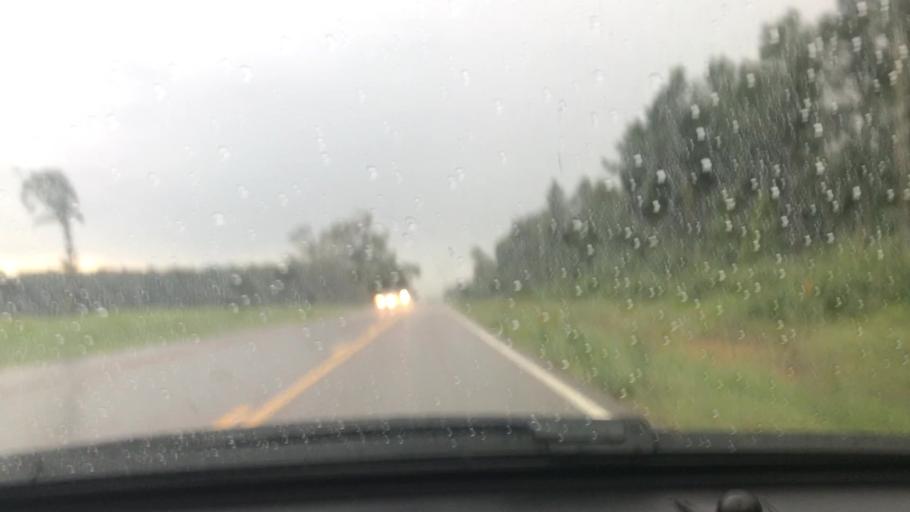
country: US
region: Mississippi
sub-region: Pike County
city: Summit
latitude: 31.3119
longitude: -90.5219
